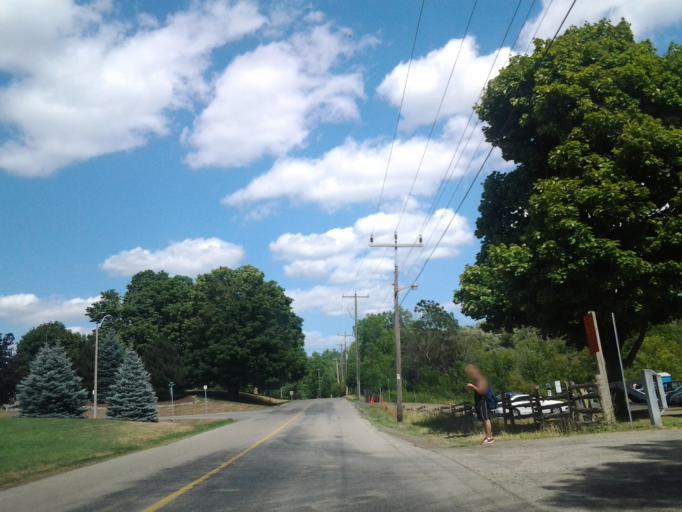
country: CA
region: Ontario
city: Ancaster
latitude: 43.2817
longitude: -79.9799
